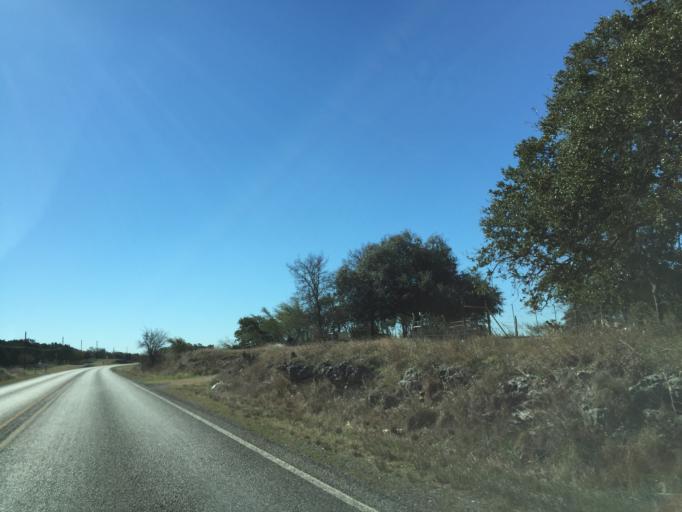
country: US
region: Texas
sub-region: Comal County
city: Garden Ridge
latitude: 29.7522
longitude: -98.3042
